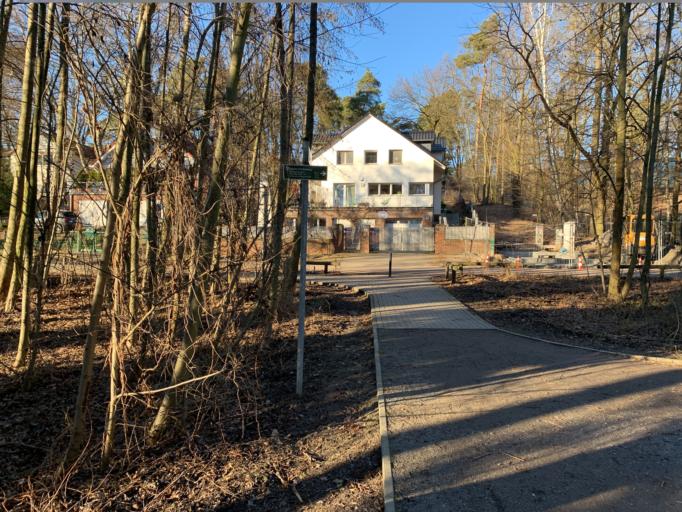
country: DE
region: Brandenburg
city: Glienicke
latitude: 52.6276
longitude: 13.3375
